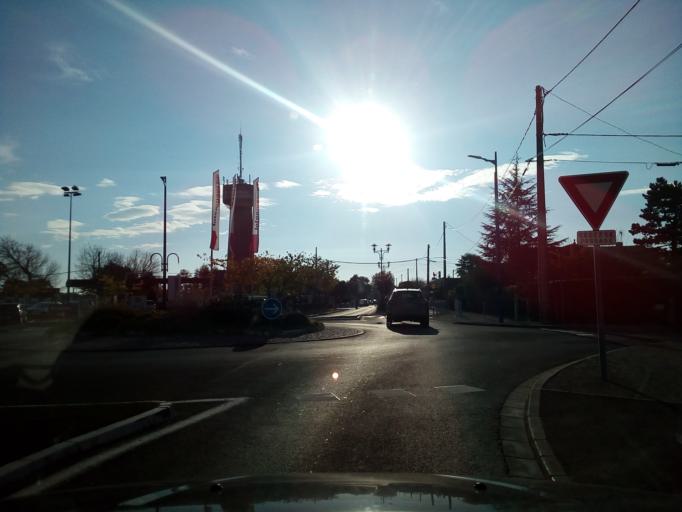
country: FR
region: Aquitaine
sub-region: Departement de la Gironde
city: Andernos-les-Bains
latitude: 44.7458
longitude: -1.0928
